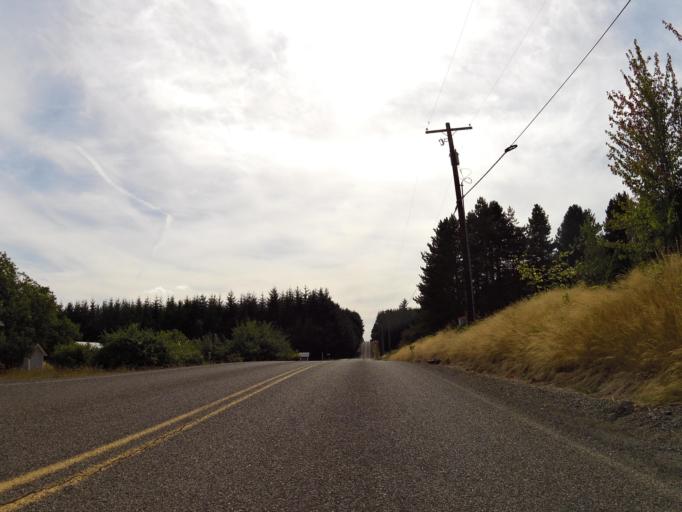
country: US
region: Washington
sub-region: Lewis County
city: Winlock
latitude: 46.5229
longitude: -122.9497
